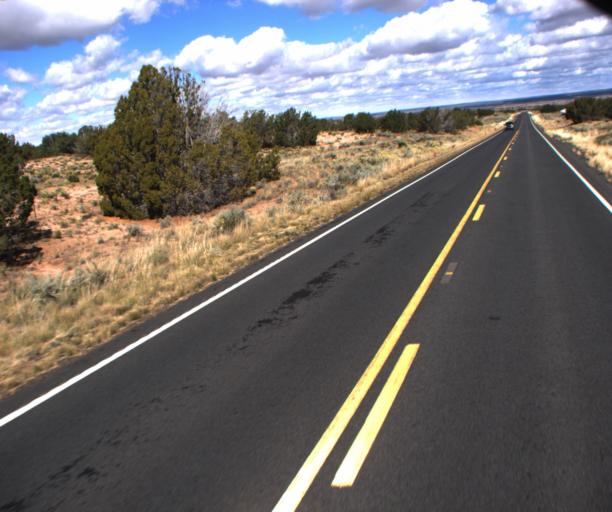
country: US
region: Arizona
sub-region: Apache County
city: Houck
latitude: 35.1457
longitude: -109.3335
